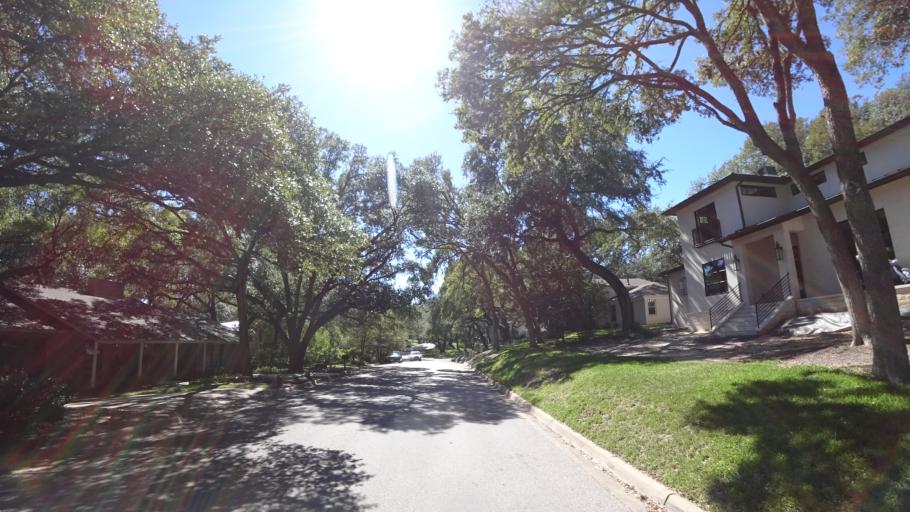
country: US
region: Texas
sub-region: Travis County
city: West Lake Hills
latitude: 30.3236
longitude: -97.7673
